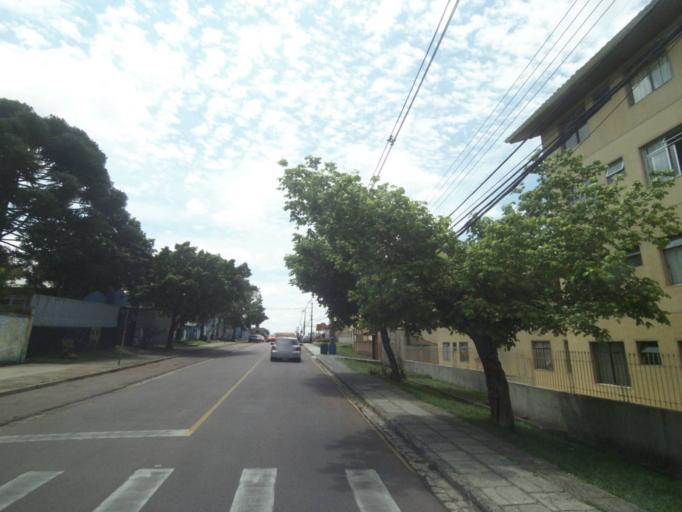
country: BR
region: Parana
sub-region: Curitiba
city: Curitiba
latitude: -25.4574
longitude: -49.3495
